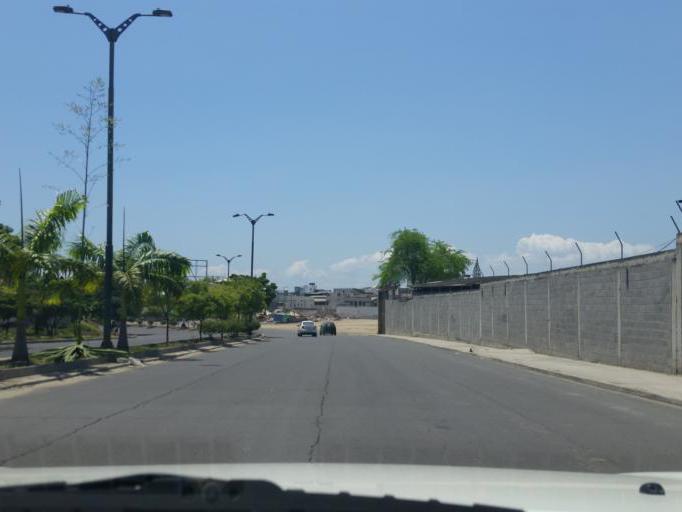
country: EC
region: Manabi
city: Manta
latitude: -0.9537
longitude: -80.7234
